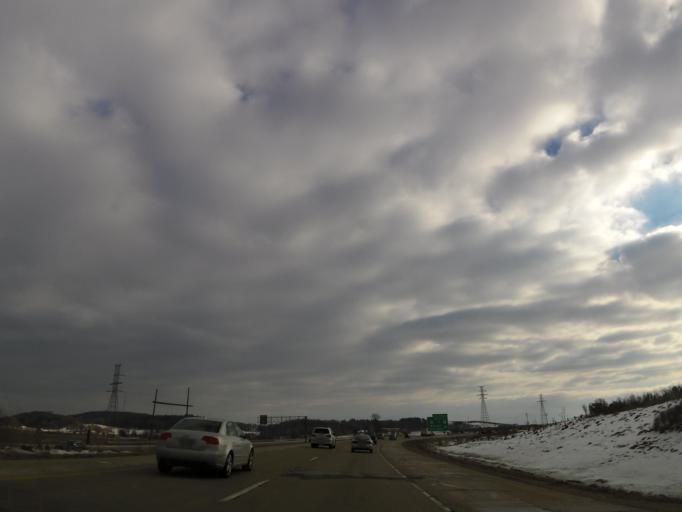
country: US
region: Wisconsin
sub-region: Columbia County
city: Portage
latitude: 43.4960
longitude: -89.4981
